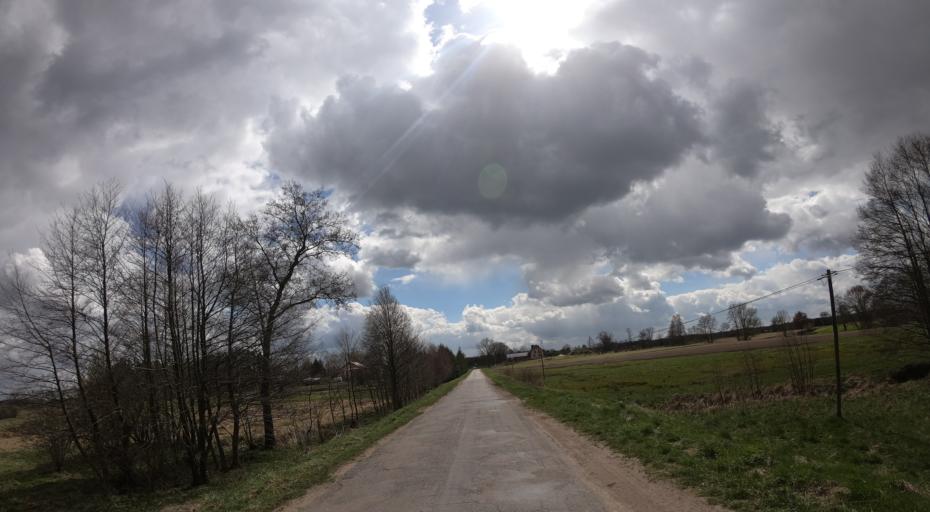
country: PL
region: West Pomeranian Voivodeship
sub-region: Powiat drawski
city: Drawsko Pomorskie
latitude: 53.5295
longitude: 15.8862
